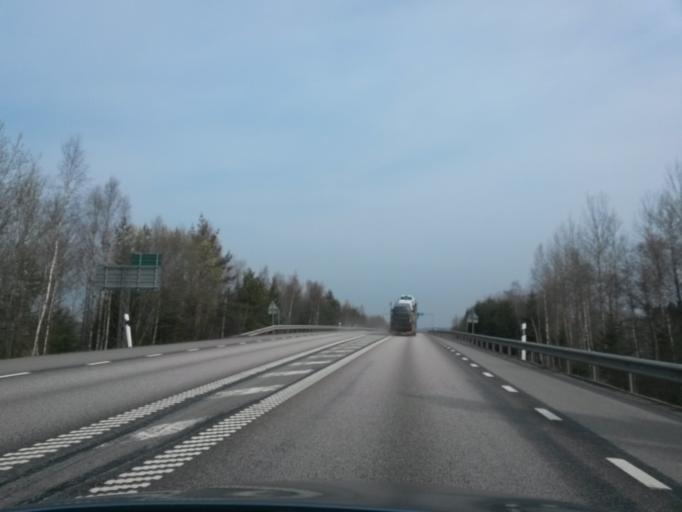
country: SE
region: Vaestra Goetaland
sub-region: Gullspangs Kommun
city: Hova
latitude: 58.8481
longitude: 14.1980
